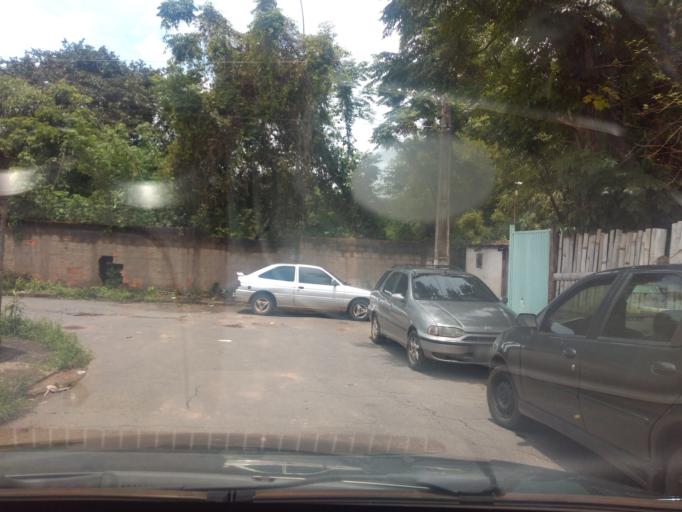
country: BR
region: Minas Gerais
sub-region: Tres Coracoes
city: Tres Coracoes
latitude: -21.6795
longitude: -45.2583
